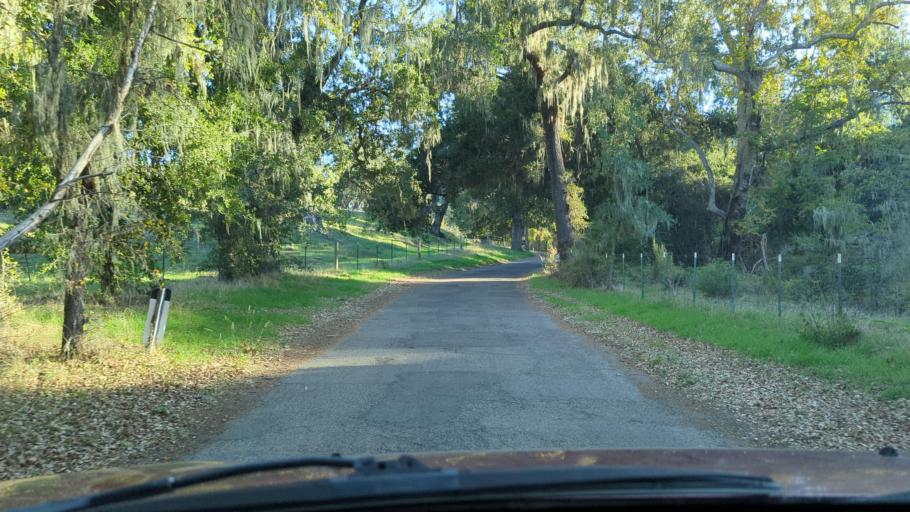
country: US
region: California
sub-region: Santa Barbara County
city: Santa Ynez
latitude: 34.5690
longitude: -120.0960
